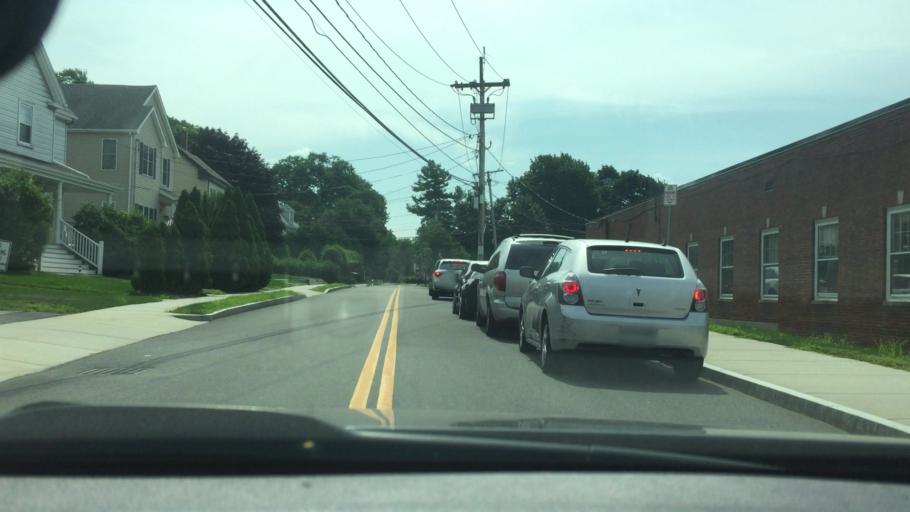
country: US
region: Massachusetts
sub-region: Norfolk County
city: Needham
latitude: 42.2946
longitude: -71.2350
